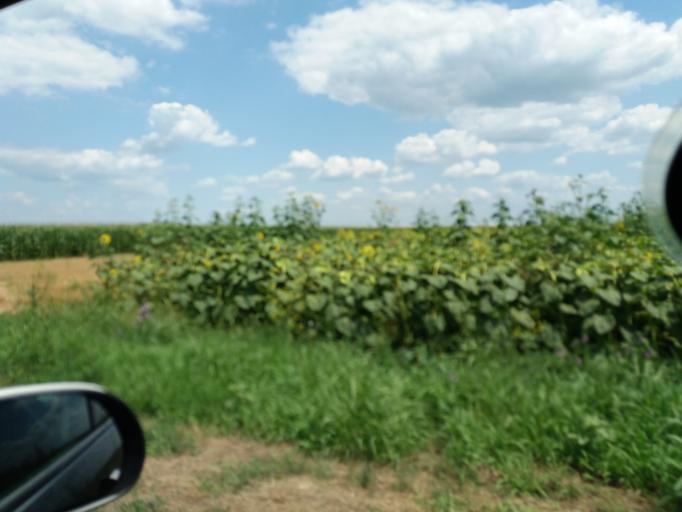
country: RS
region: Autonomna Pokrajina Vojvodina
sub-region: Sremski Okrug
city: Pecinci
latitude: 44.8884
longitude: 19.9629
